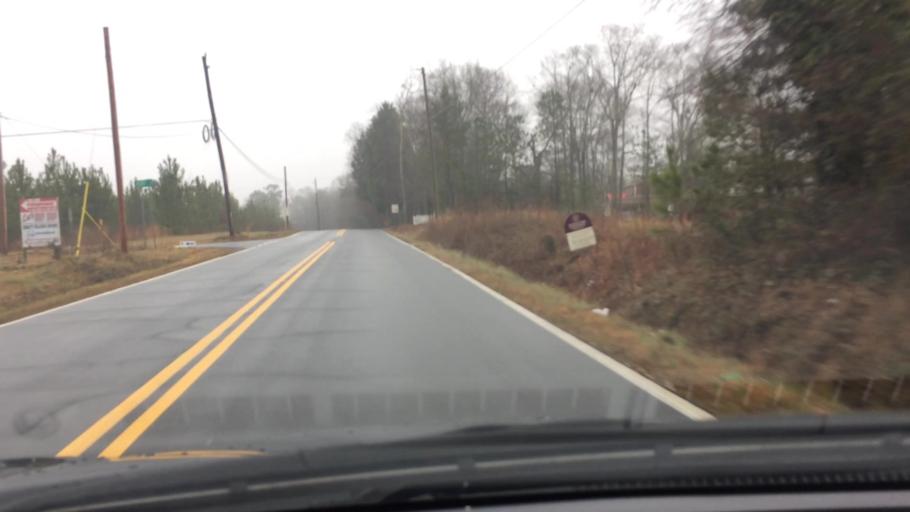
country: US
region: South Carolina
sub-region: Anderson County
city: Williamston
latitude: 34.6393
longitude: -82.4812
